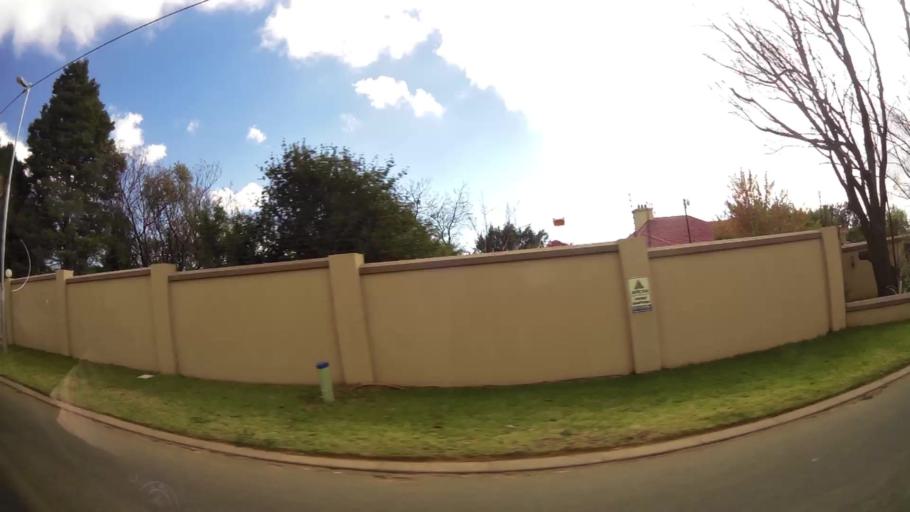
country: ZA
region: Gauteng
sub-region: West Rand District Municipality
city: Muldersdriseloop
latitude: -26.0932
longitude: 27.8599
